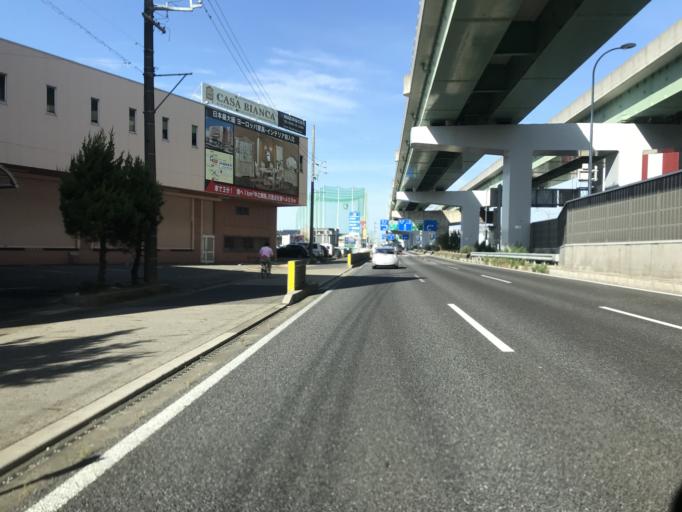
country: JP
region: Aichi
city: Iwakura
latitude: 35.2541
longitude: 136.8432
